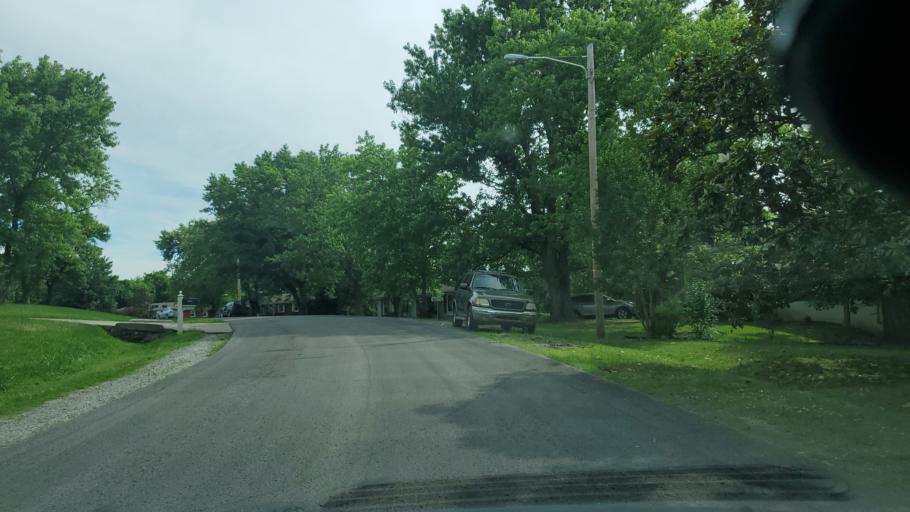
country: US
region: Tennessee
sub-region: Davidson County
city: Lakewood
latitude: 36.2054
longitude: -86.6847
